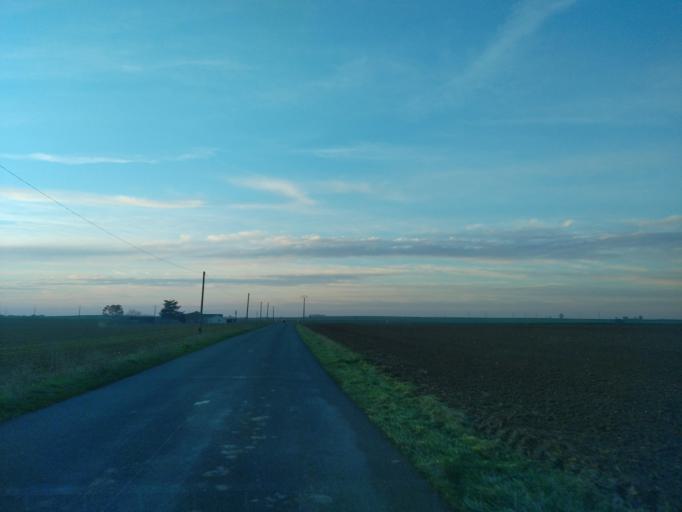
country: FR
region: Pays de la Loire
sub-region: Departement de la Vendee
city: Vix
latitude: 46.3998
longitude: -0.8472
